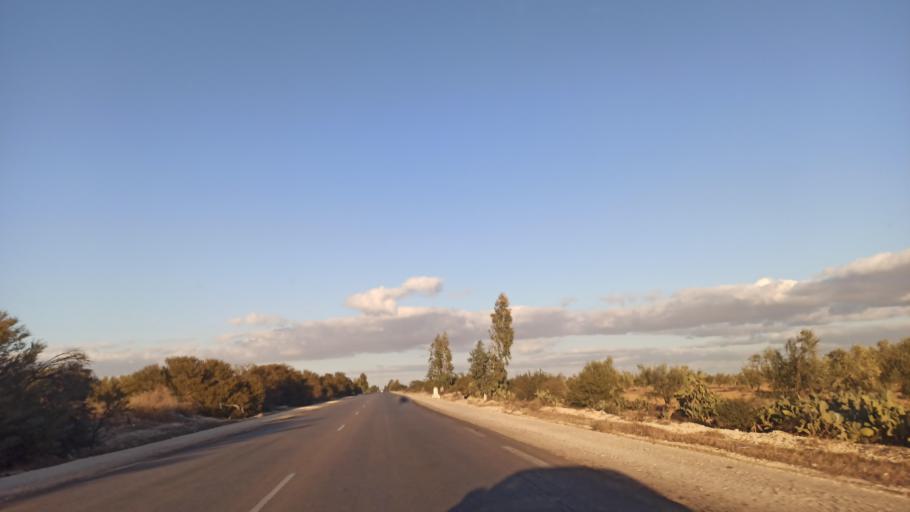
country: TN
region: Al Qayrawan
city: Sbikha
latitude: 35.8616
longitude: 10.2072
